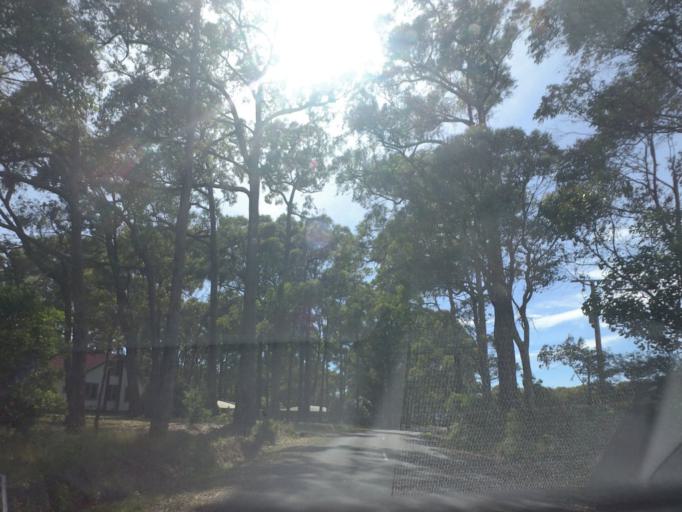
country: AU
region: Victoria
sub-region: Nillumbik
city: Saint Andrews
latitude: -37.5110
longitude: 145.3594
